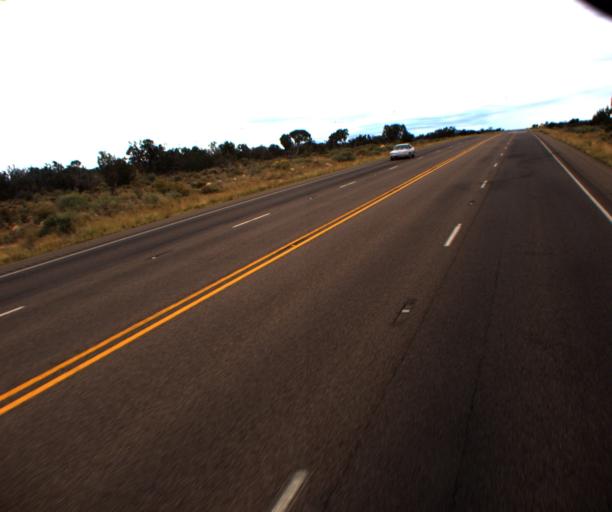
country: US
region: Arizona
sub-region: Navajo County
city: Snowflake
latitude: 34.6391
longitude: -110.0958
